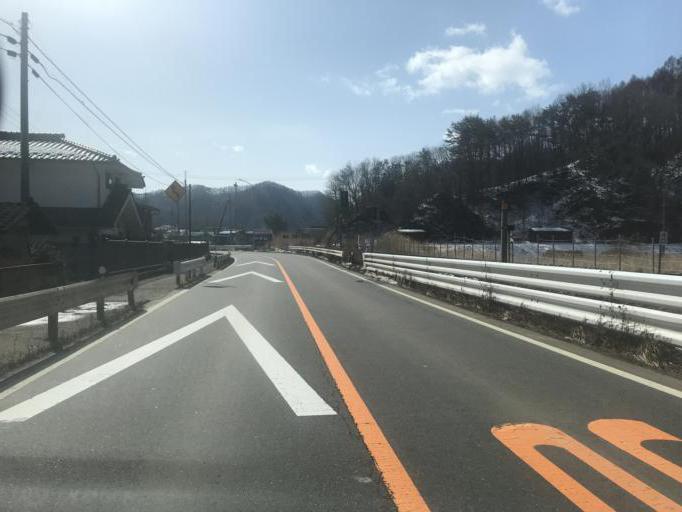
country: JP
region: Nagano
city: Saku
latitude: 36.0264
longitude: 138.4872
